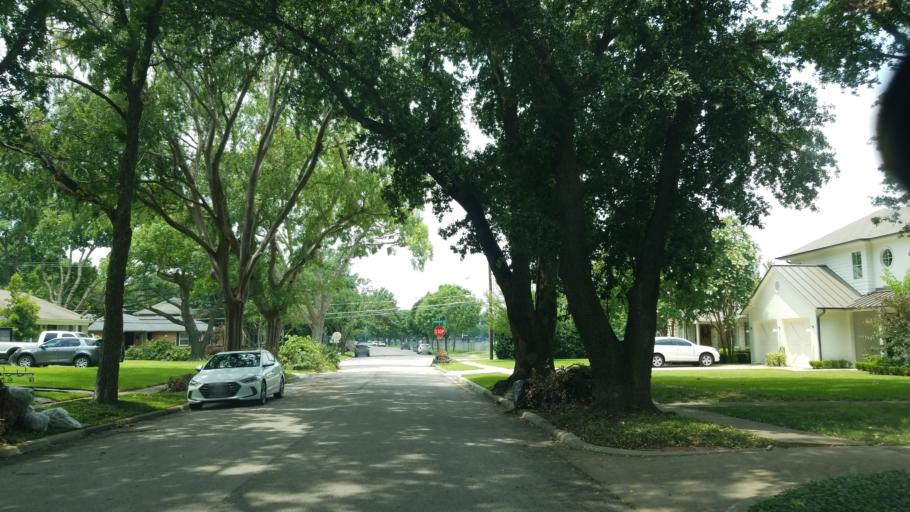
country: US
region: Texas
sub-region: Dallas County
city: University Park
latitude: 32.8474
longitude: -96.8182
